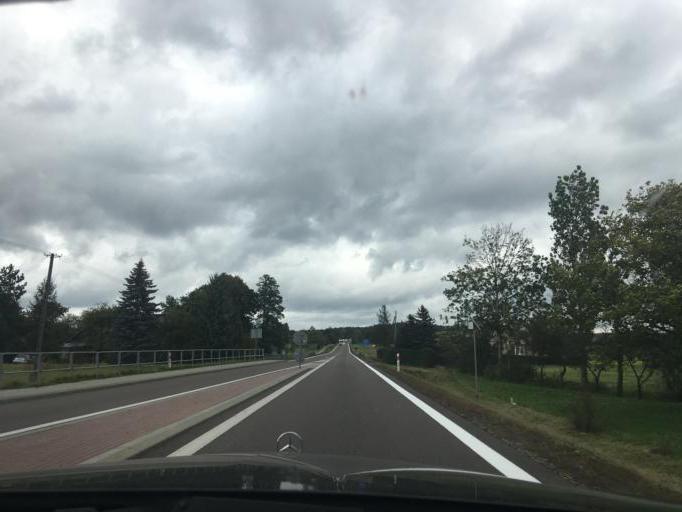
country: PL
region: Subcarpathian Voivodeship
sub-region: Powiat brzozowski
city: Jablonica Polska
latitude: 49.7004
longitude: 21.8809
